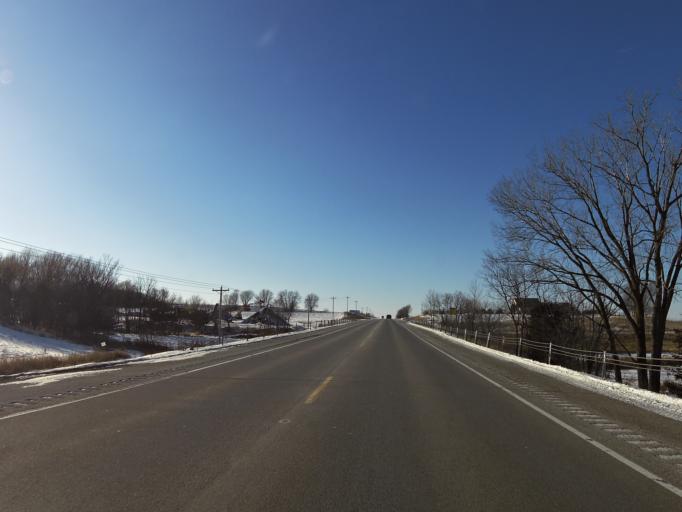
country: US
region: Minnesota
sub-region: Le Sueur County
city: New Prague
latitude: 44.5436
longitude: -93.5155
